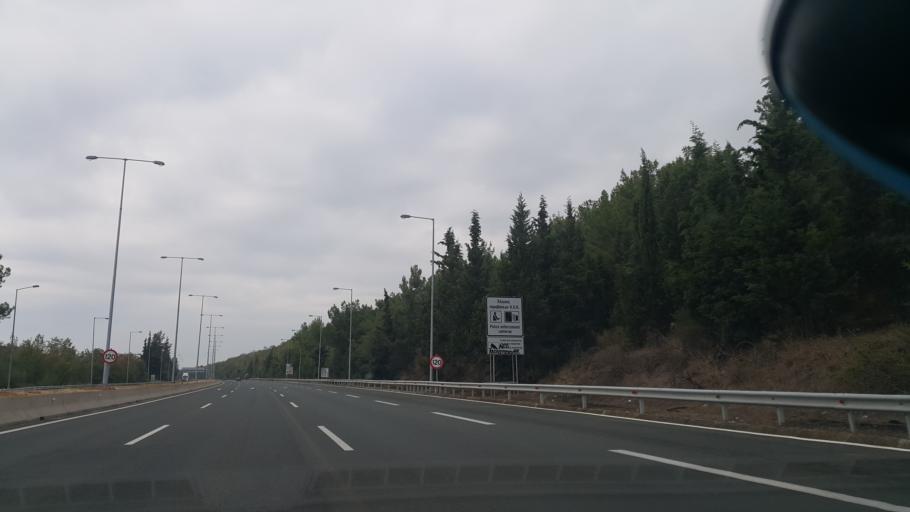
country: GR
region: Central Macedonia
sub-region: Nomos Pierias
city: Makrygialos
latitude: 40.4139
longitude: 22.5919
